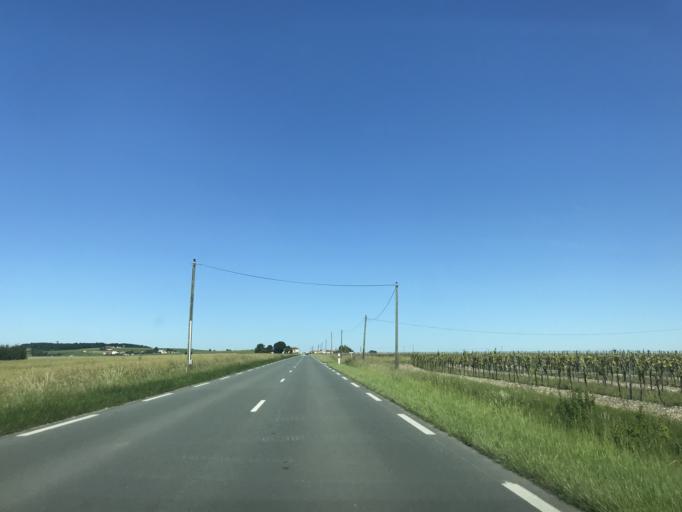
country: FR
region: Poitou-Charentes
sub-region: Departement de la Charente
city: Segonzac
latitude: 45.5335
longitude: -0.3179
